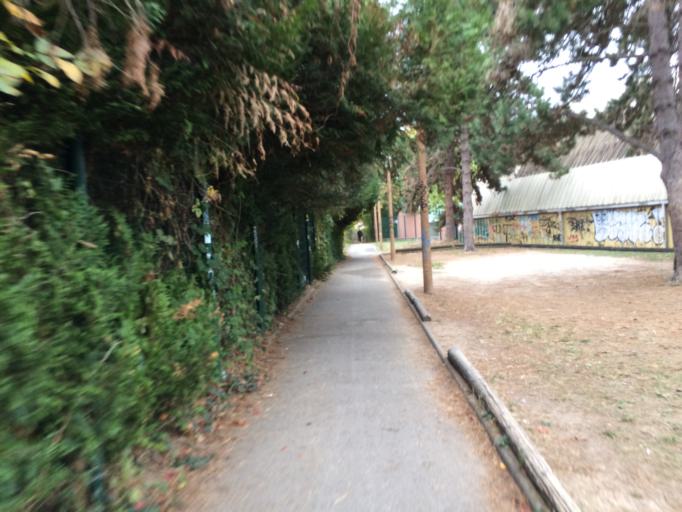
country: FR
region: Ile-de-France
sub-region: Departement de l'Essonne
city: Villebon-sur-Yvette
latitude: 48.7079
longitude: 2.2482
